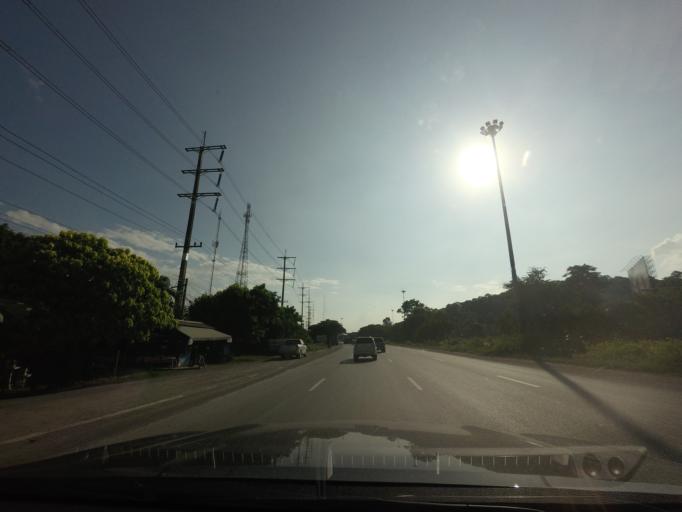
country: TH
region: Sara Buri
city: Chaloem Phra Kiat
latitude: 14.6659
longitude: 100.8897
